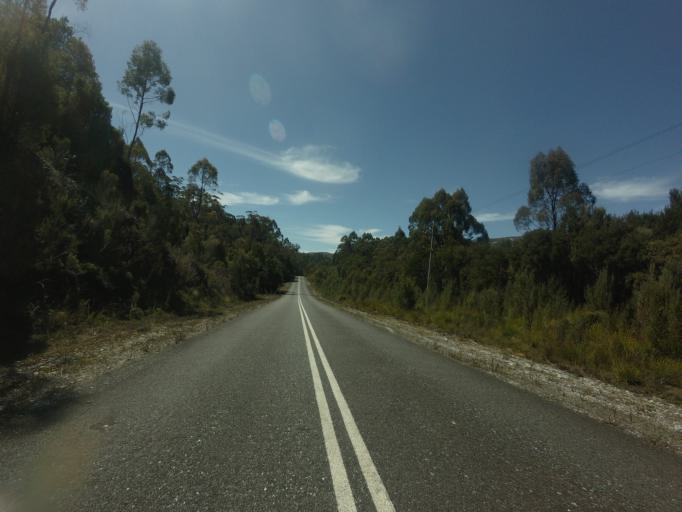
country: AU
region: Tasmania
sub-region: West Coast
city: Queenstown
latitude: -42.7723
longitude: 146.0426
